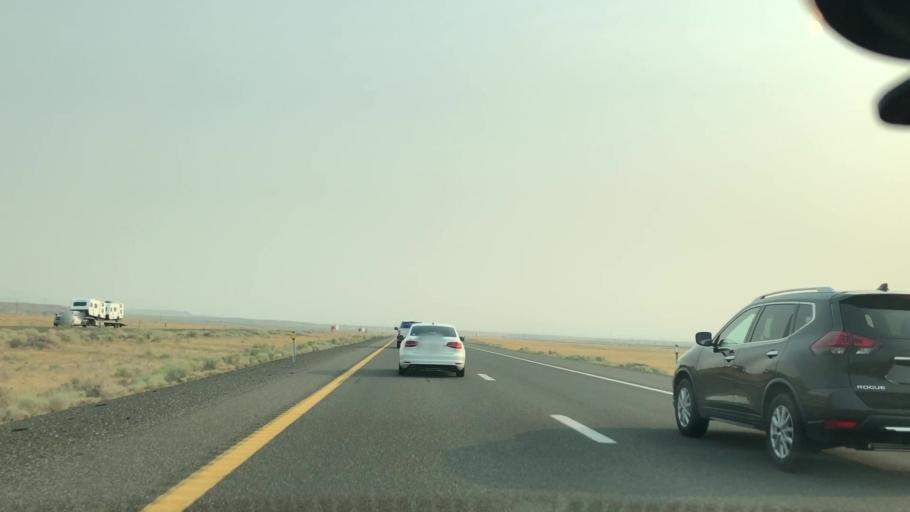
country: US
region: Nevada
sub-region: Pershing County
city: Lovelock
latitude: 40.0166
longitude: -118.6759
